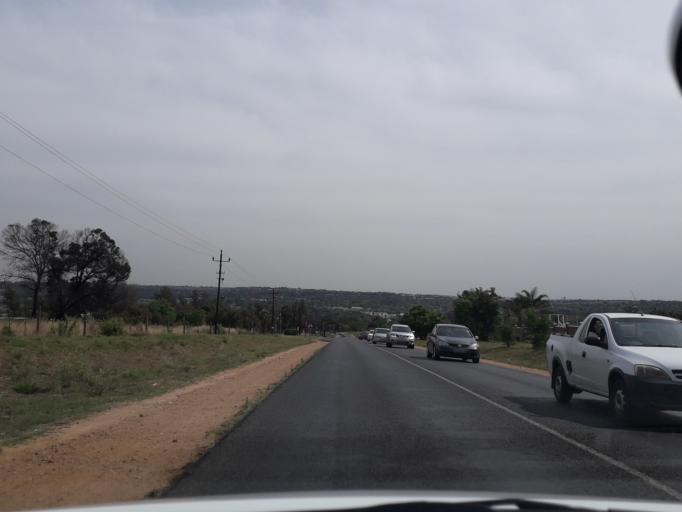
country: ZA
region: Gauteng
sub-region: City of Johannesburg Metropolitan Municipality
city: Diepsloot
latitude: -25.9992
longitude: 28.0442
